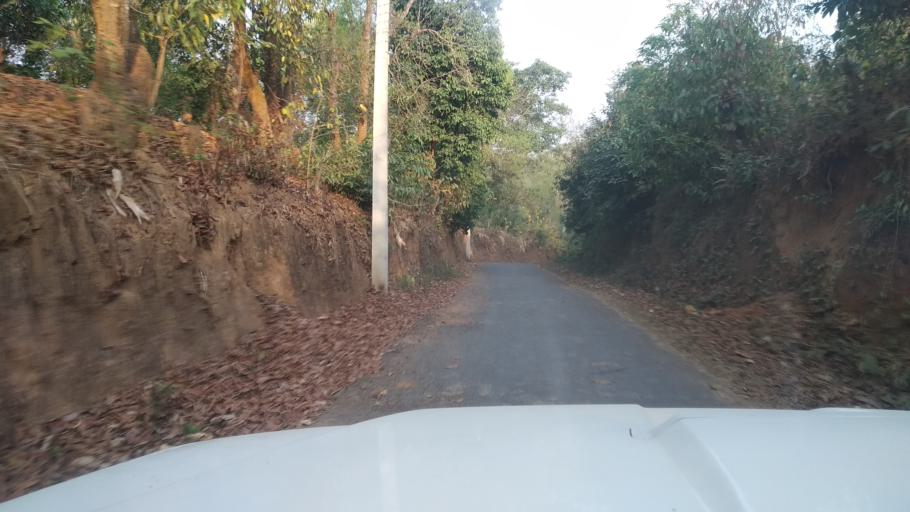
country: IN
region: Tripura
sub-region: South Tripura
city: Belonia
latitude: 23.3181
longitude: 91.3218
